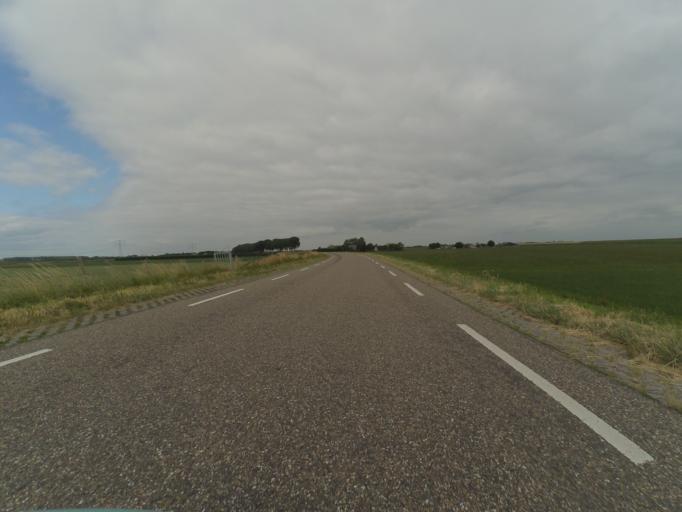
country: NL
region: Zeeland
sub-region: Gemeente Reimerswaal
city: Yerseke
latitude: 51.4589
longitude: 4.0713
